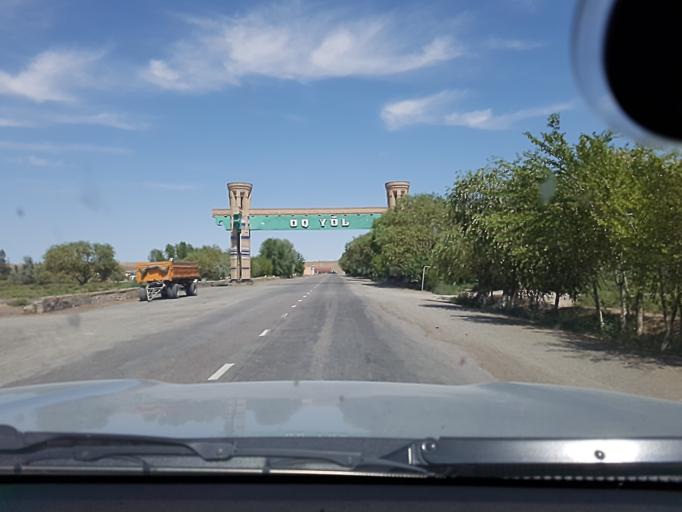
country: UZ
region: Karakalpakstan
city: Mang'it Shahri
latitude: 42.2425
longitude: 60.1491
